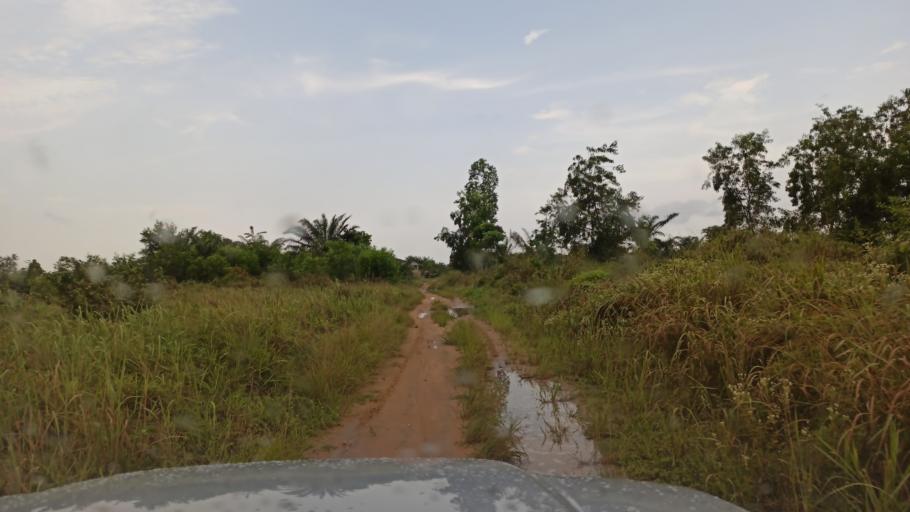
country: BJ
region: Queme
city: Porto-Novo
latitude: 6.4539
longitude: 2.6679
